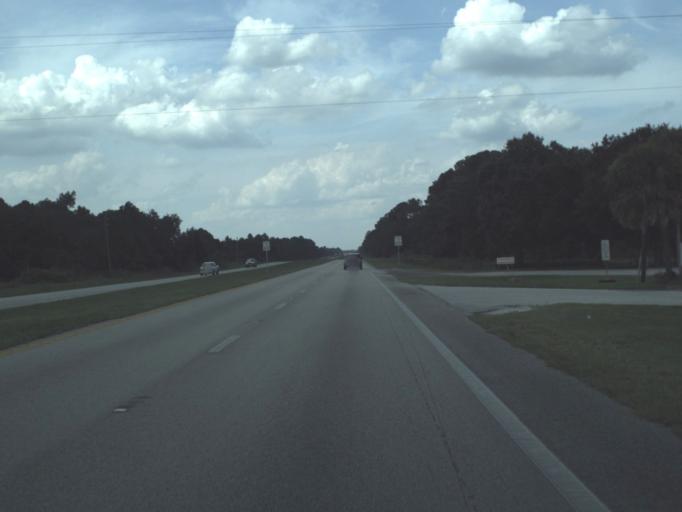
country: US
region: Florida
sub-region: Polk County
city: Frostproof
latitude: 27.7363
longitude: -81.5743
